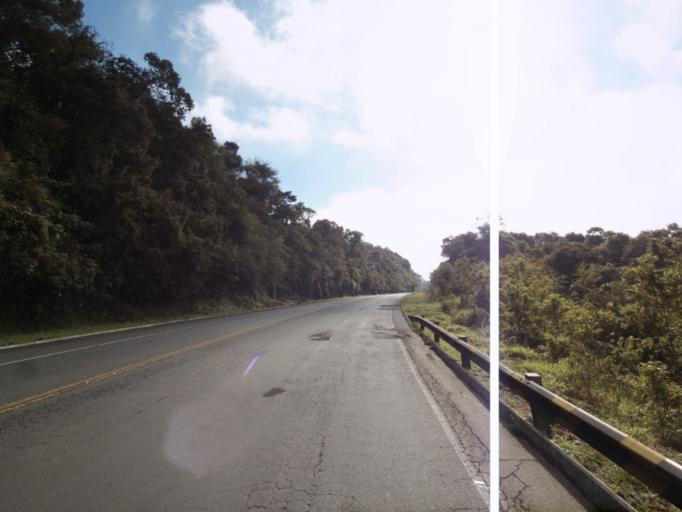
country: BR
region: Rio Grande do Sul
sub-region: Frederico Westphalen
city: Frederico Westphalen
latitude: -27.1320
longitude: -53.2132
